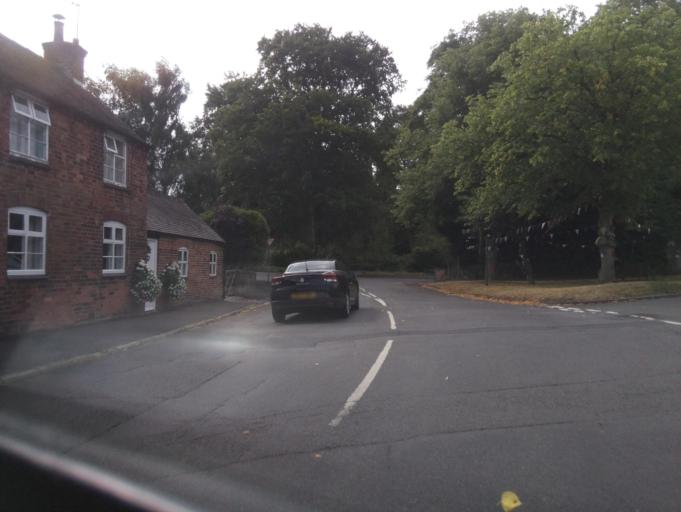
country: GB
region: England
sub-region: Derbyshire
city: Ilkeston
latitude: 52.9372
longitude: -1.3094
